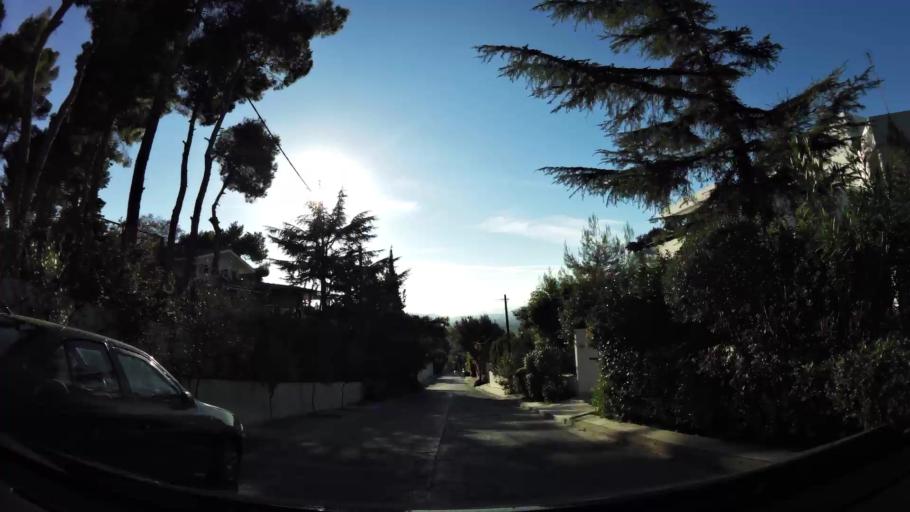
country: GR
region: Attica
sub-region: Nomarchia Athinas
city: Ekali
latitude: 38.0982
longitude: 23.8305
